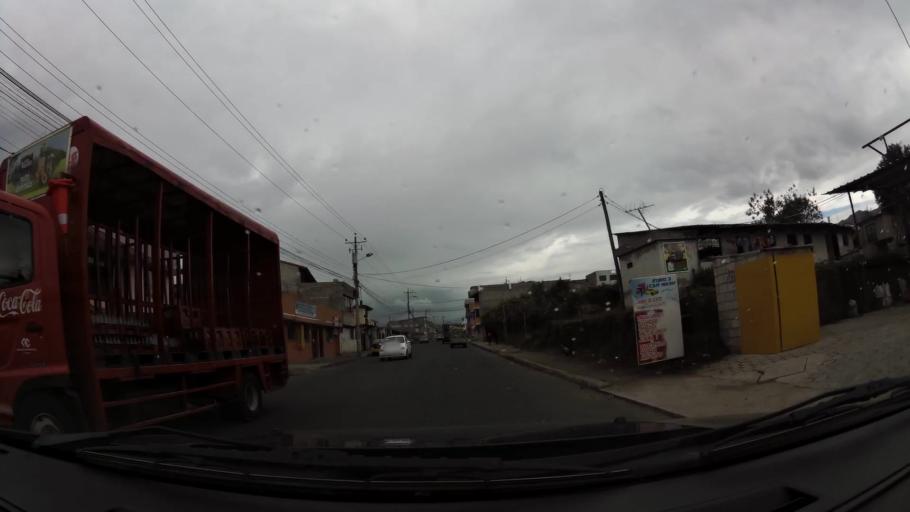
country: EC
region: Pichincha
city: Sangolqui
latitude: -0.3365
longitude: -78.5536
